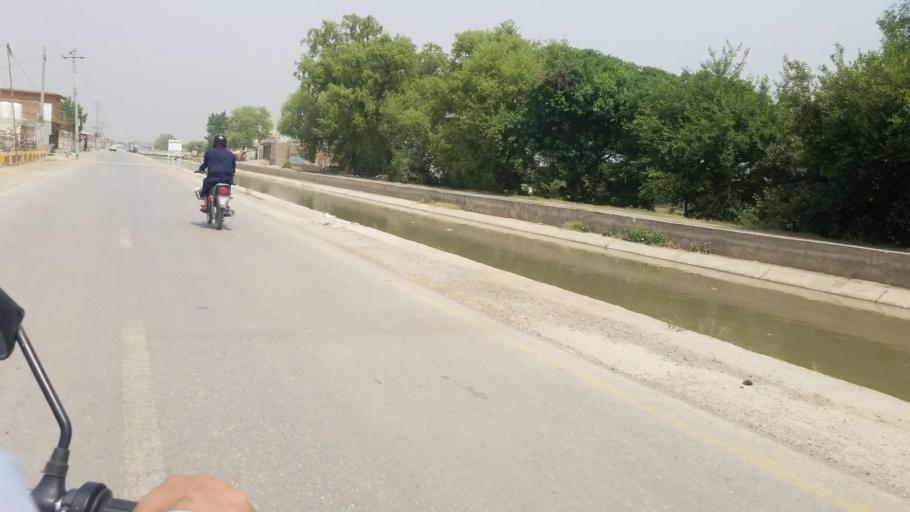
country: PK
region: Khyber Pakhtunkhwa
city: Peshawar
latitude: 33.9504
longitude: 71.5530
